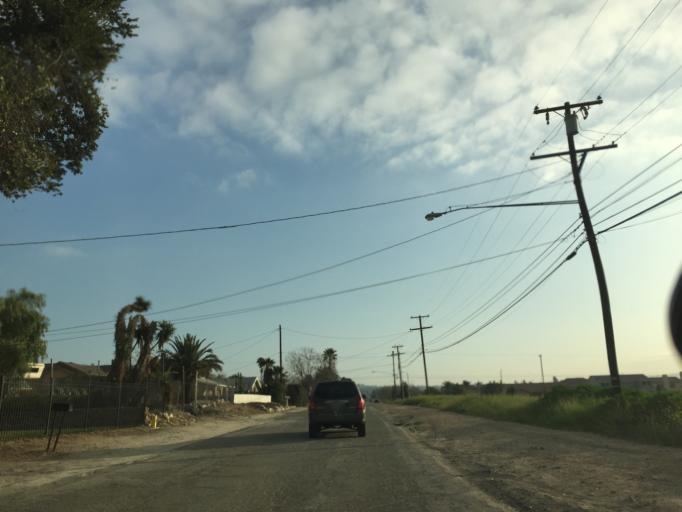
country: US
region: California
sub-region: San Bernardino County
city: Mentone
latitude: 34.0764
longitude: -117.1389
